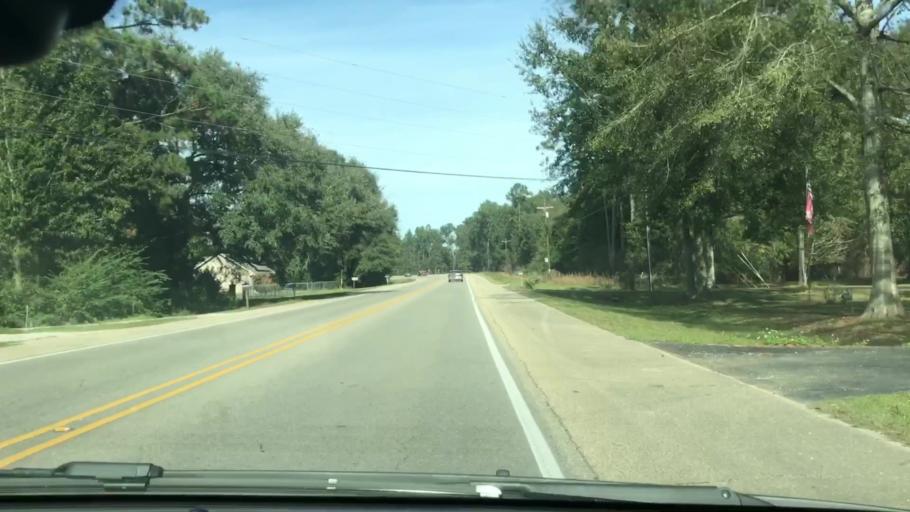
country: US
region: Louisiana
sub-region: Saint Tammany Parish
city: Pearl River
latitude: 30.4284
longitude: -89.7870
